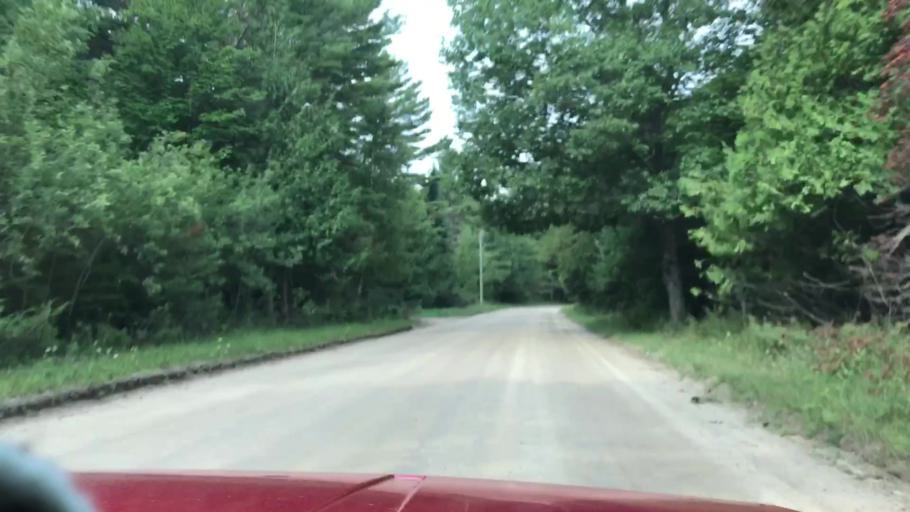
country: US
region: Michigan
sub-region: Charlevoix County
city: Charlevoix
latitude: 45.7278
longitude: -85.5345
